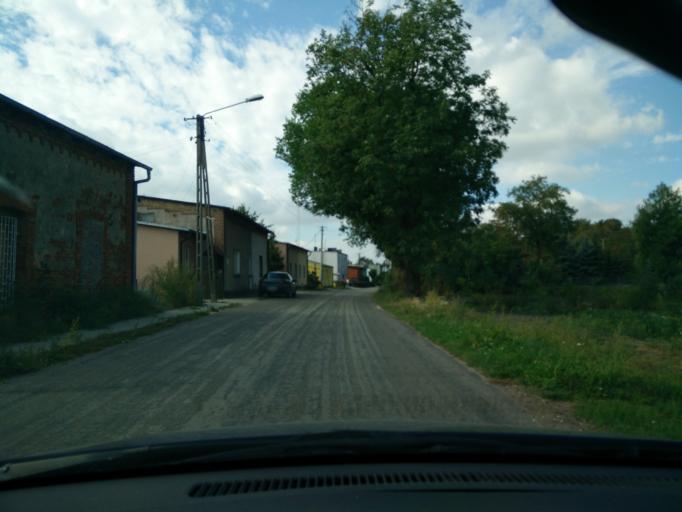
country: PL
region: Greater Poland Voivodeship
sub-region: Powiat sredzki
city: Dominowo
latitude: 52.2264
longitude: 17.3675
